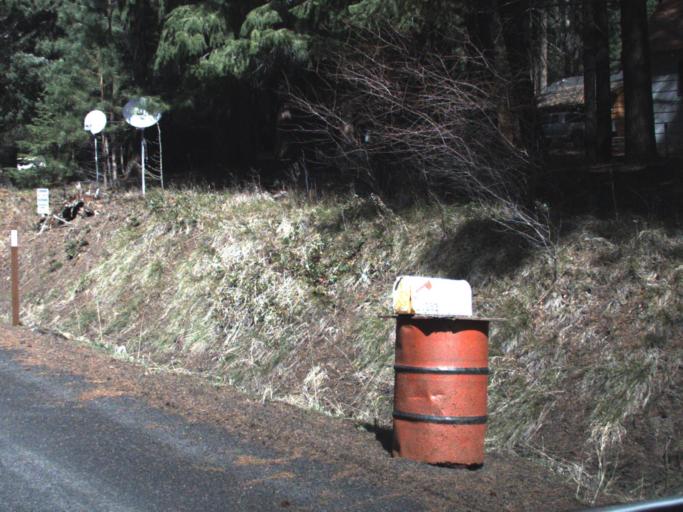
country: US
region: Washington
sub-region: Kittitas County
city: Cle Elum
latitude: 46.9440
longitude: -121.0666
